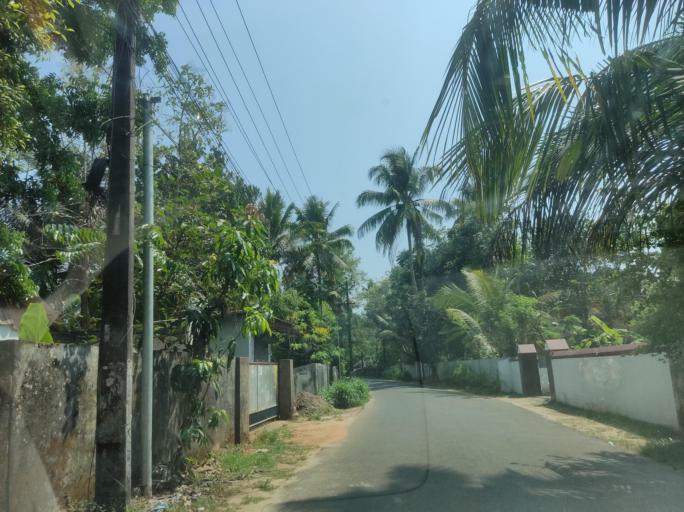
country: IN
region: Kerala
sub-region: Alappuzha
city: Vayalar
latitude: 9.6995
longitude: 76.3037
